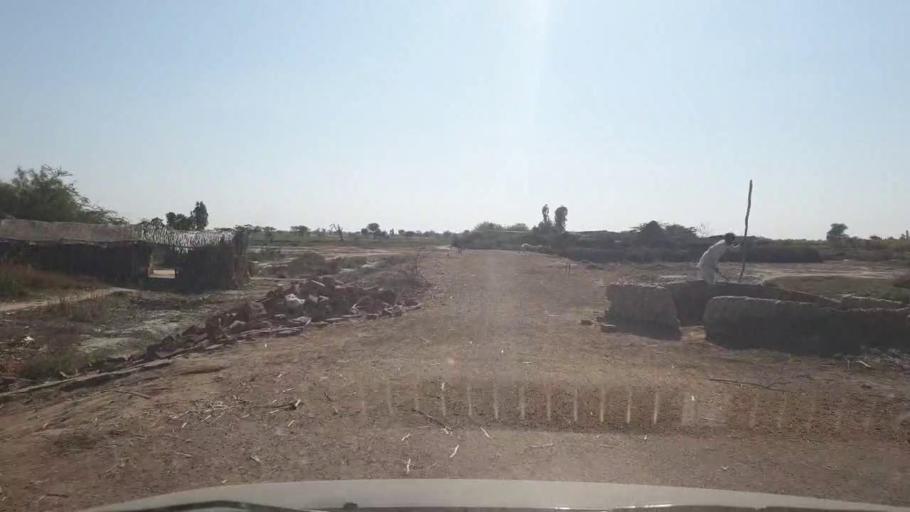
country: PK
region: Sindh
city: Samaro
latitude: 25.3719
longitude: 69.3307
